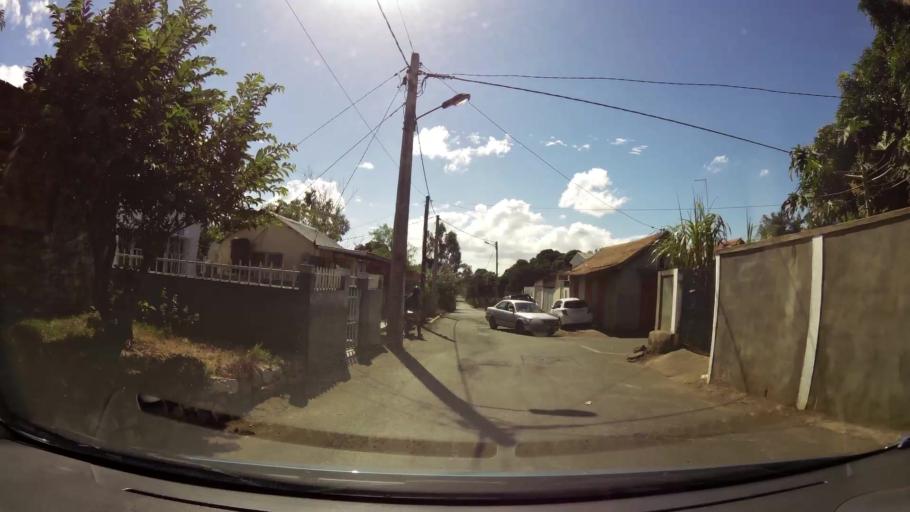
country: MU
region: Black River
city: Cascavelle
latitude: -20.2637
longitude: 57.4127
